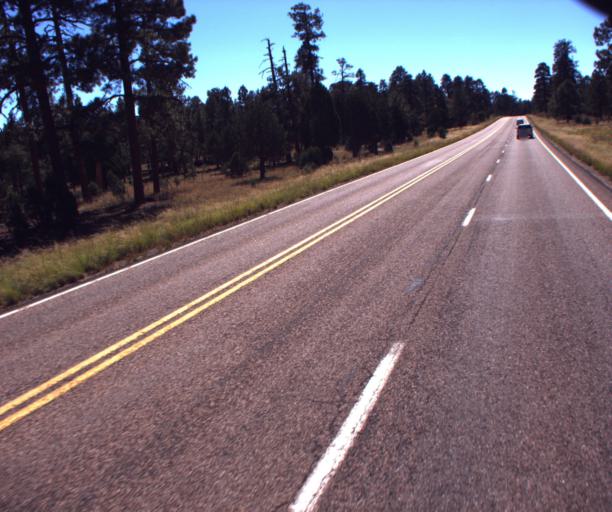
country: US
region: Arizona
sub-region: Navajo County
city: Heber-Overgaard
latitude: 34.3897
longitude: -110.6712
